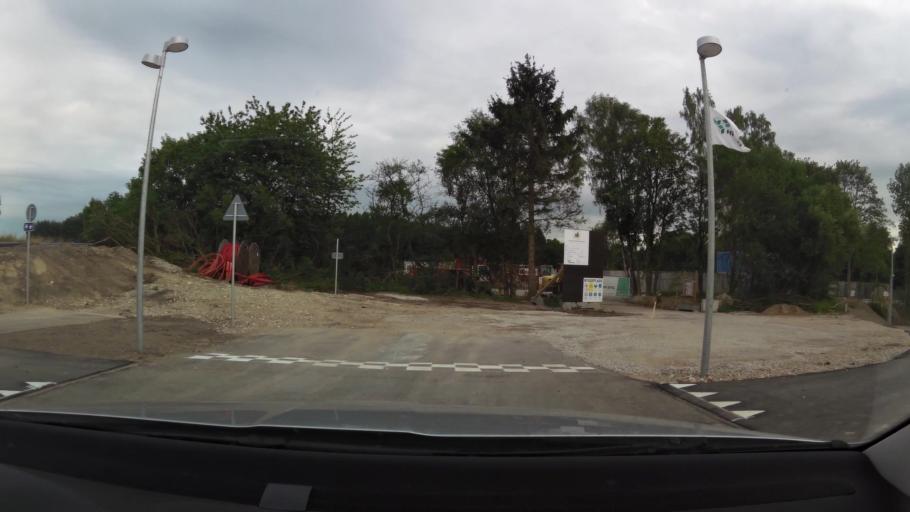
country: DK
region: Capital Region
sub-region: Allerod Kommune
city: Blovstrod
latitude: 55.8639
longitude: 12.3735
